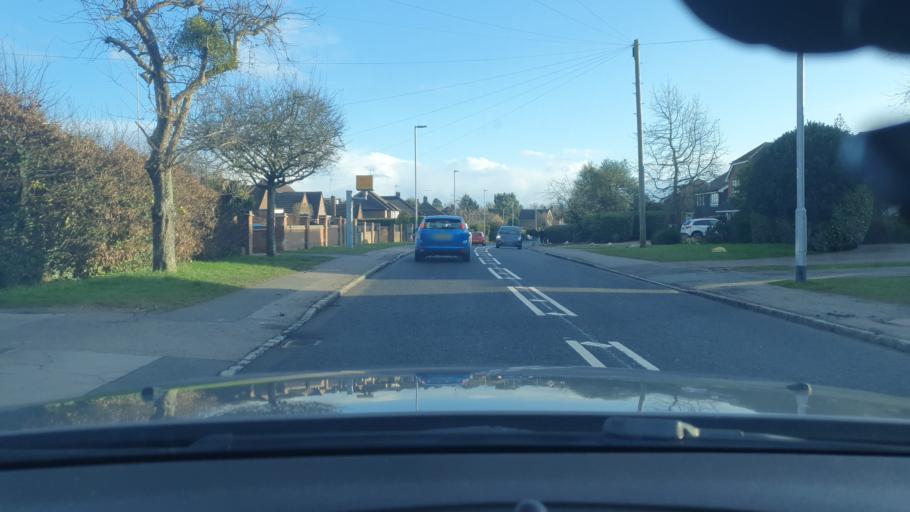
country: GB
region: England
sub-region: Wokingham
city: Woodley
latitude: 51.4573
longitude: -0.8986
